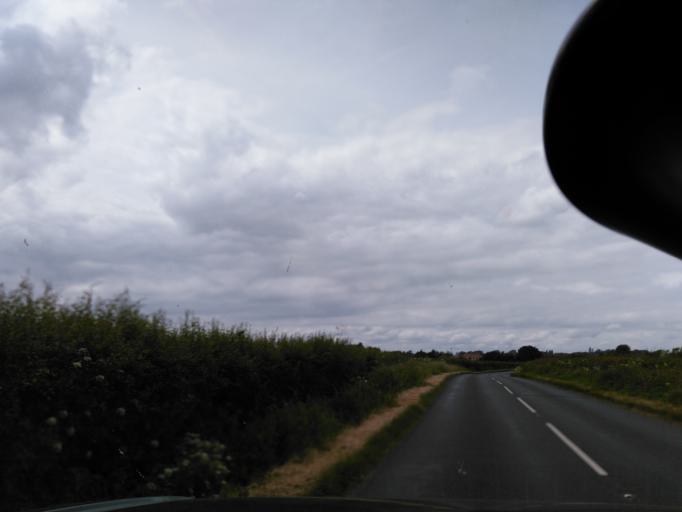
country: GB
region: England
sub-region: Wiltshire
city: Bulkington
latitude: 51.3316
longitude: -2.0756
